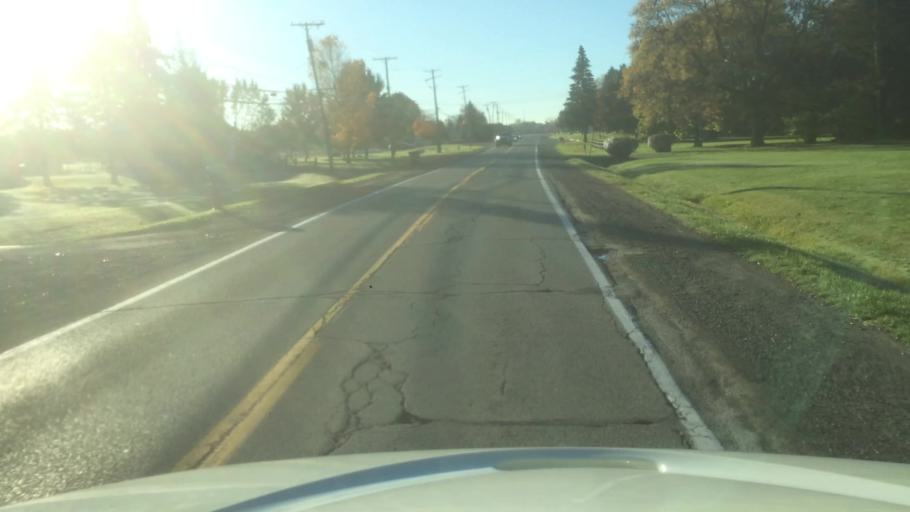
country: US
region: Michigan
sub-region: Macomb County
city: Shelby
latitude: 42.6780
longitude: -82.9444
